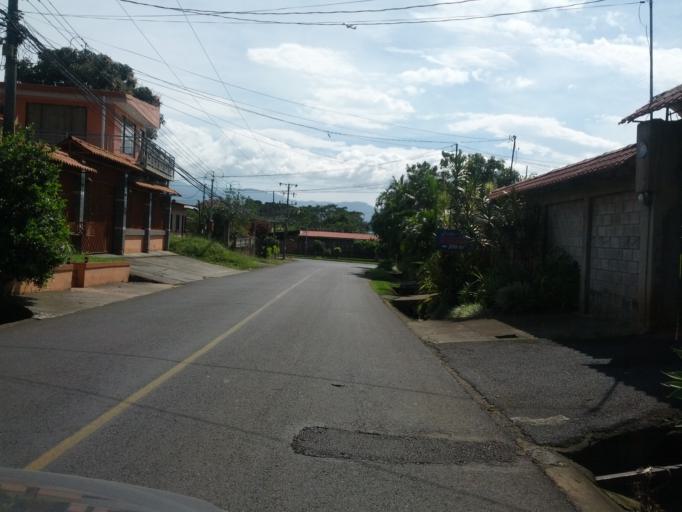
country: CR
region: Heredia
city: Llorente
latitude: 10.0195
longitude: -84.1791
